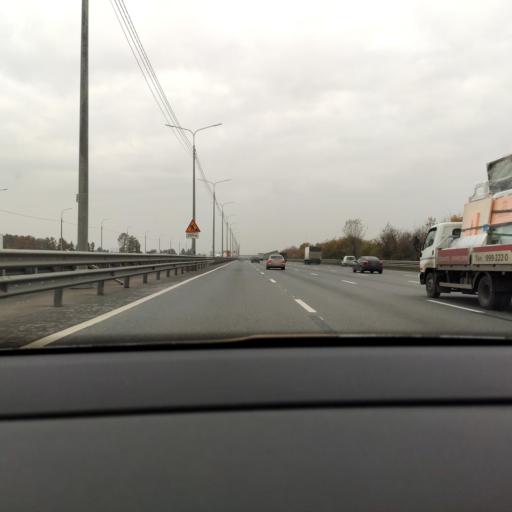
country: RU
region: Moskovskaya
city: Lesnyye Polyany
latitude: 55.9771
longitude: 37.8562
